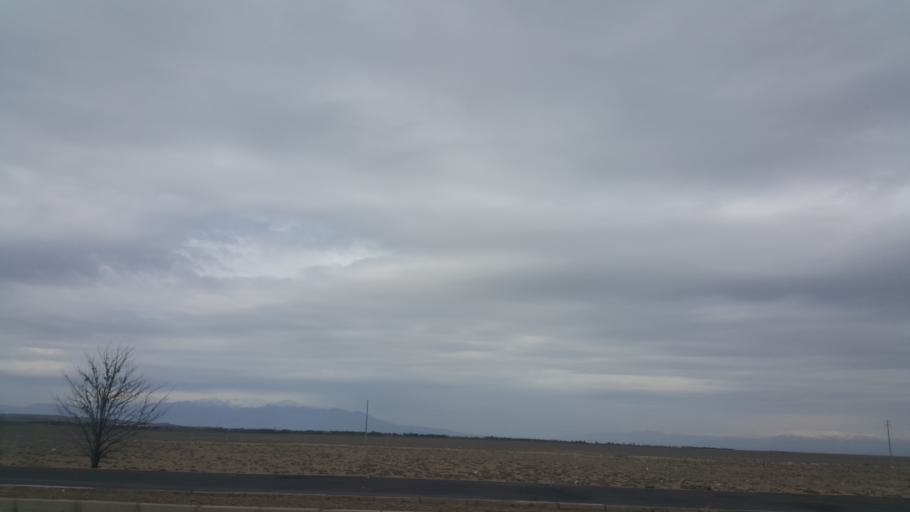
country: TR
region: Nigde
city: Altunhisar
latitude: 37.7786
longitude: 34.2384
